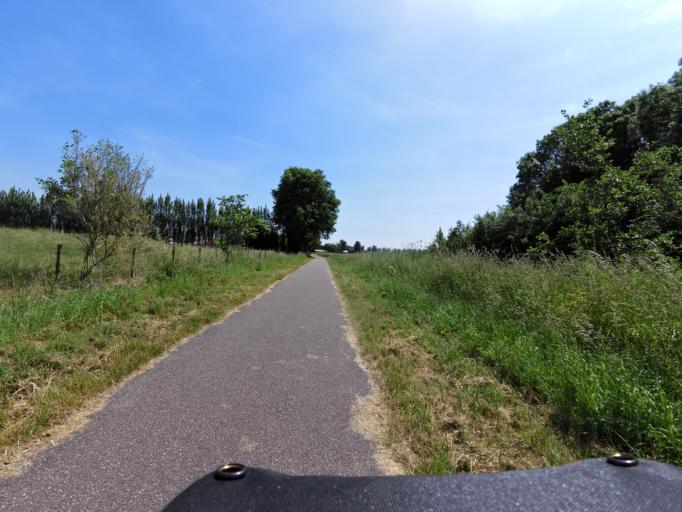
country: NL
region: South Holland
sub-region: Gemeente Spijkenisse
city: Spijkenisse
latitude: 51.7970
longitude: 4.3080
